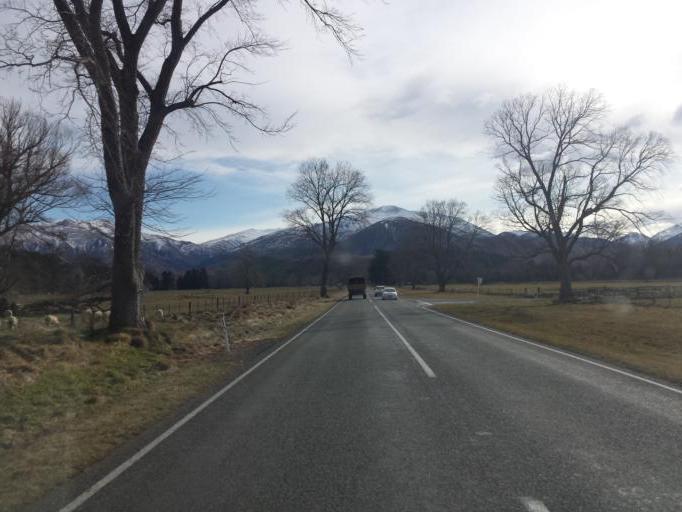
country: NZ
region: Canterbury
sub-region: Timaru District
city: Pleasant Point
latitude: -44.0393
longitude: 170.7519
